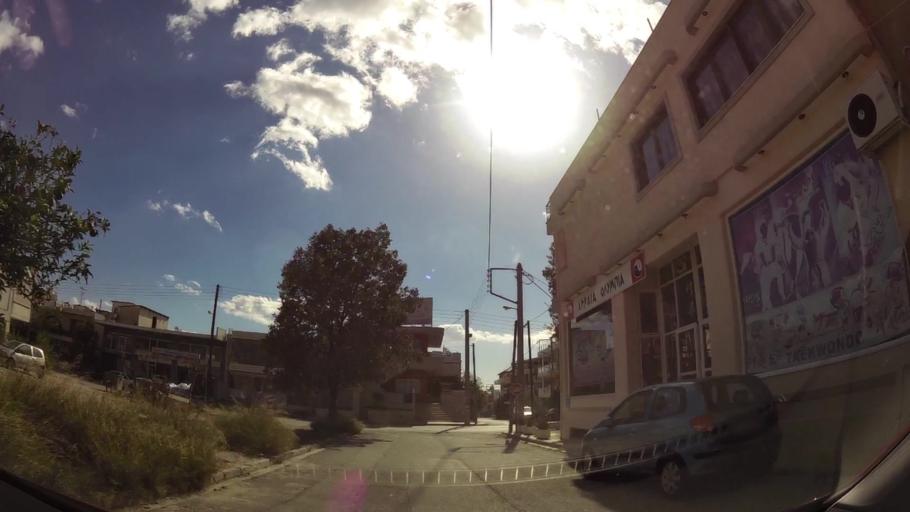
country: GR
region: Attica
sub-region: Nomarchia Anatolikis Attikis
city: Acharnes
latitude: 38.0953
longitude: 23.7336
